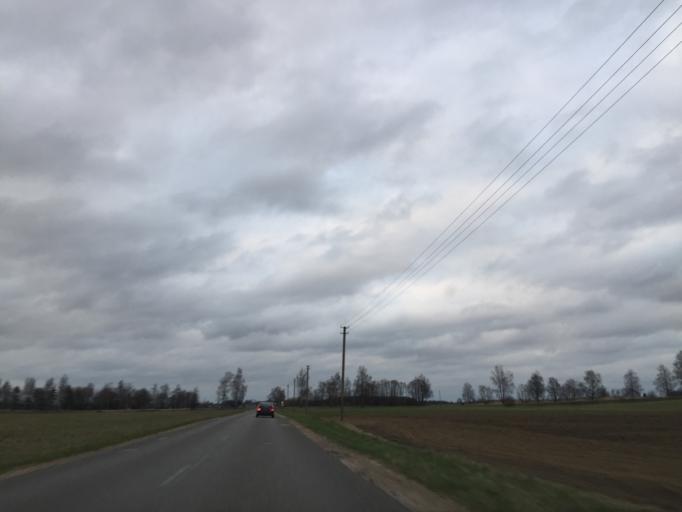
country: LT
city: Skaudvile
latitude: 55.4894
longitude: 22.5882
